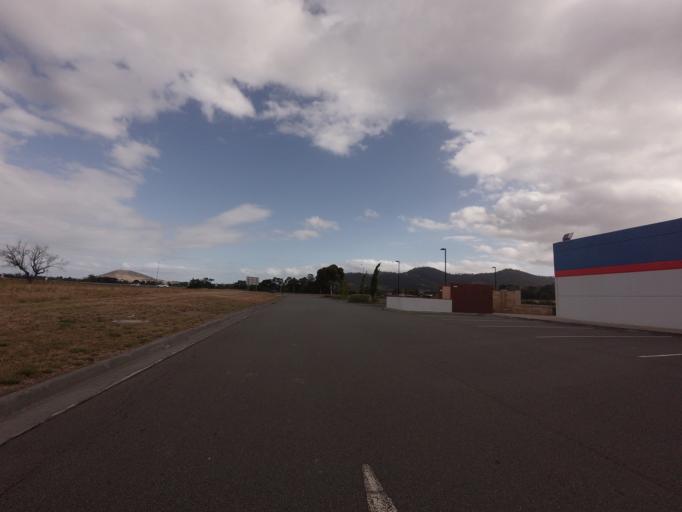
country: AU
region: Tasmania
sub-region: Clarence
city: Cambridge
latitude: -42.8339
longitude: 147.4710
